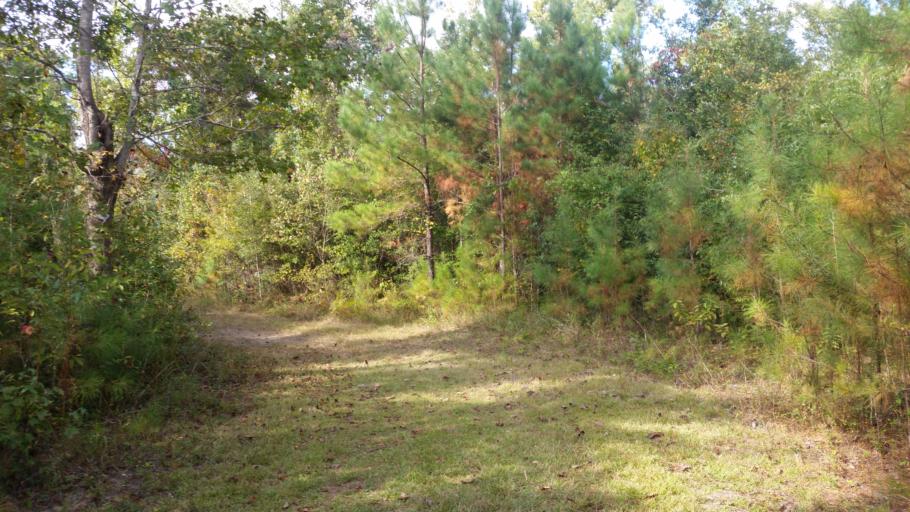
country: US
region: Mississippi
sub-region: Stone County
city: Wiggins
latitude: 30.9962
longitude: -89.0555
